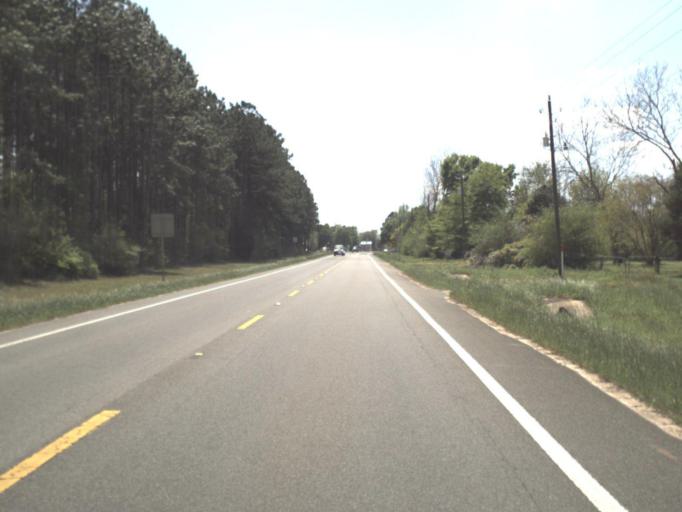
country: US
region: Florida
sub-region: Okaloosa County
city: Crestview
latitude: 30.8038
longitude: -86.6801
